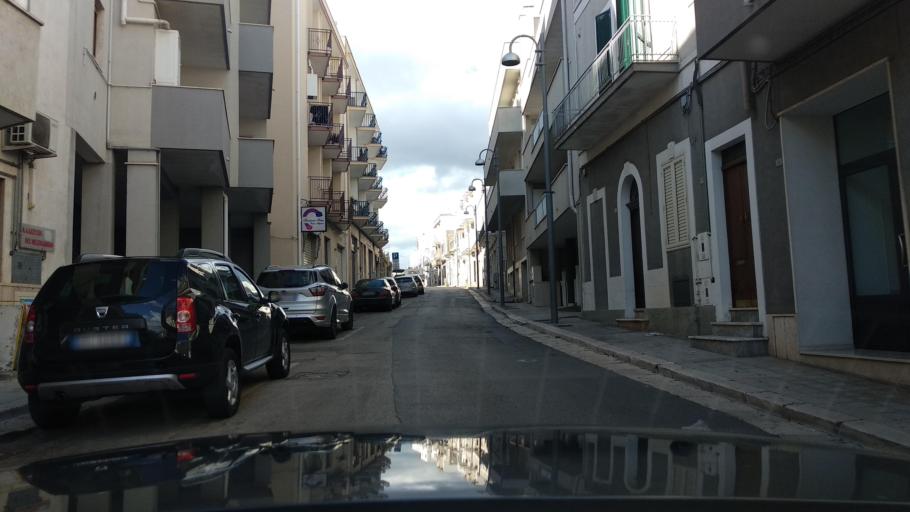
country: IT
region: Apulia
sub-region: Provincia di Brindisi
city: Cisternino
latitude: 40.7419
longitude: 17.4289
